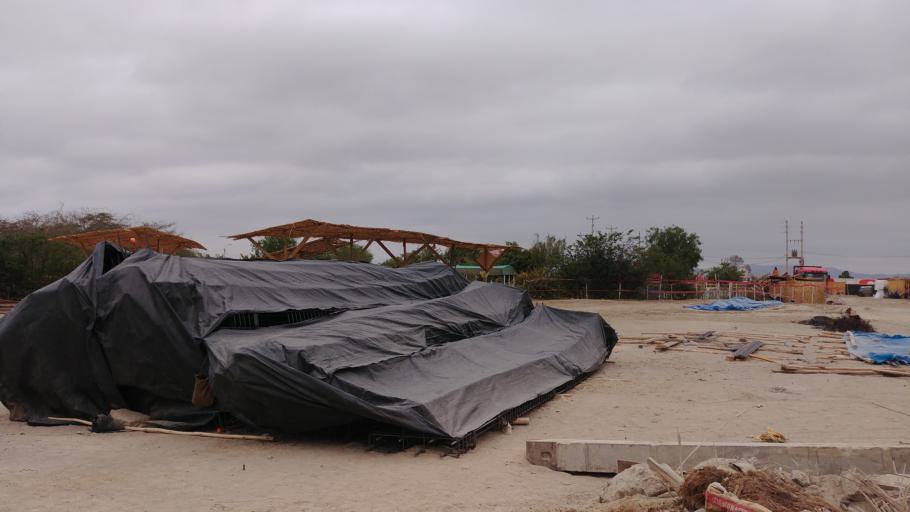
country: PE
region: Ica
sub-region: Provincia de Pisco
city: Villa Tupac Amaru
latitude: -13.8346
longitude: -76.1421
